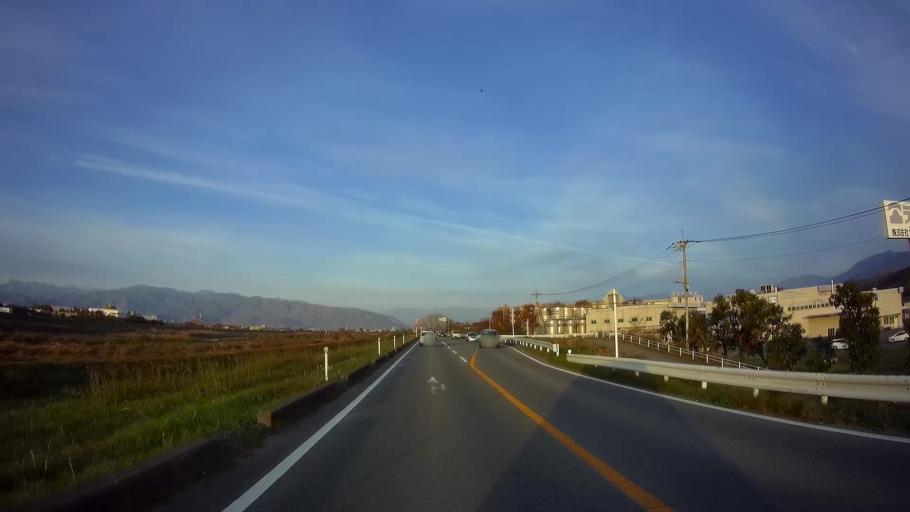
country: JP
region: Yamanashi
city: Kofu-shi
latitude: 35.5906
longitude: 138.5597
